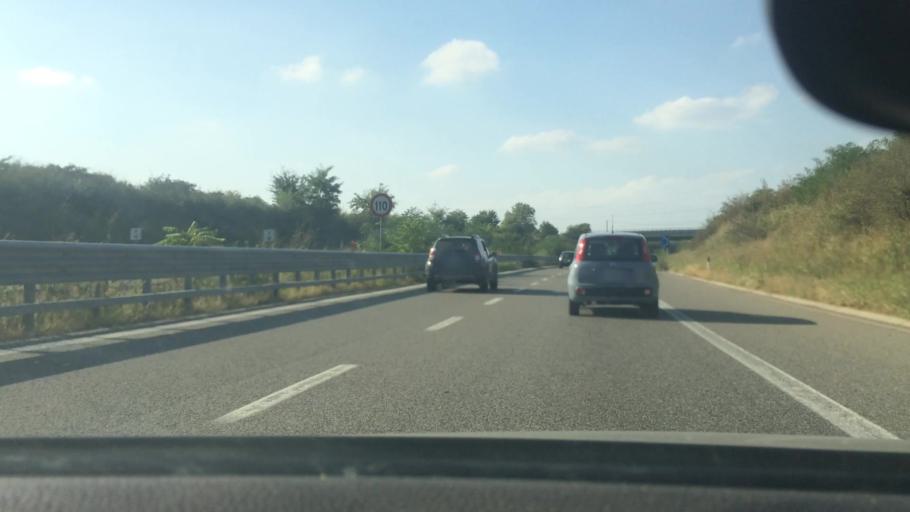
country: IT
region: Lombardy
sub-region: Citta metropolitana di Milano
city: Buscate
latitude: 45.5301
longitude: 8.8044
